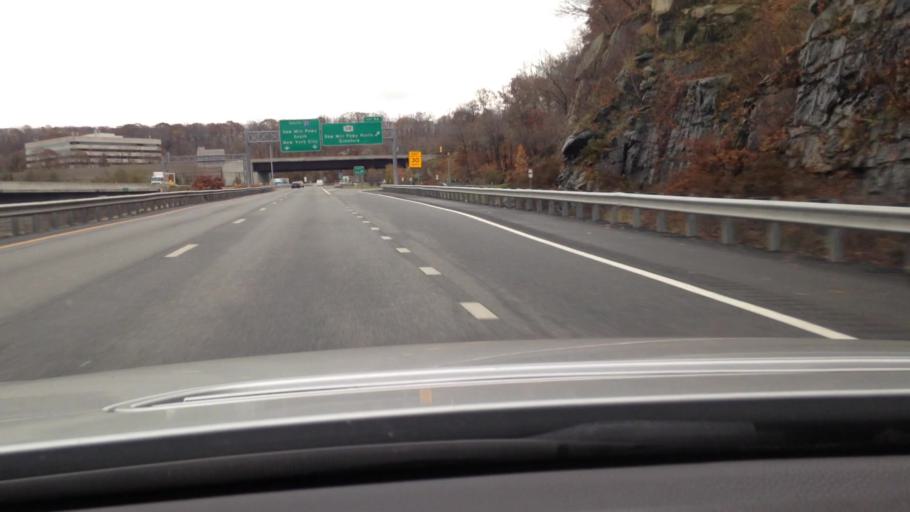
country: US
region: New York
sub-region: Westchester County
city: Elmsford
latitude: 41.0588
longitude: -73.8386
